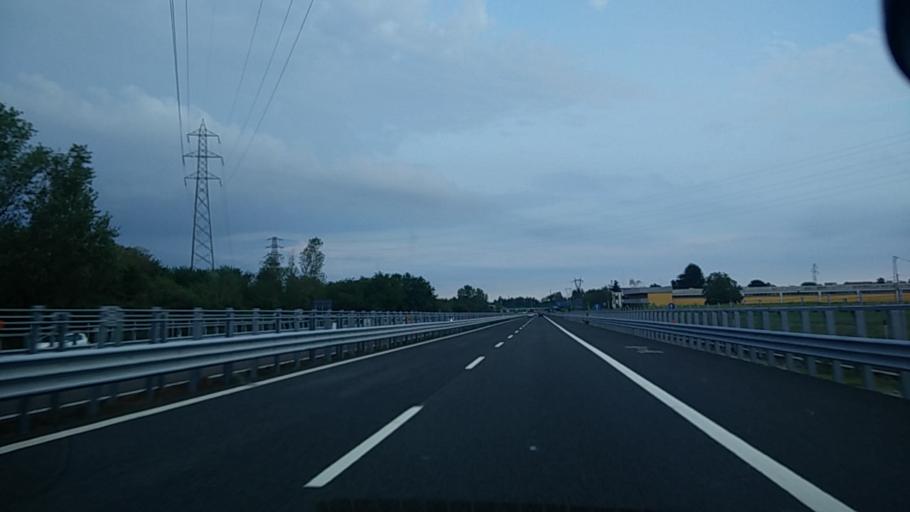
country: IT
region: Friuli Venezia Giulia
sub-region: Provincia di Udine
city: Pasian di Prato
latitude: 46.0557
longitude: 13.2009
